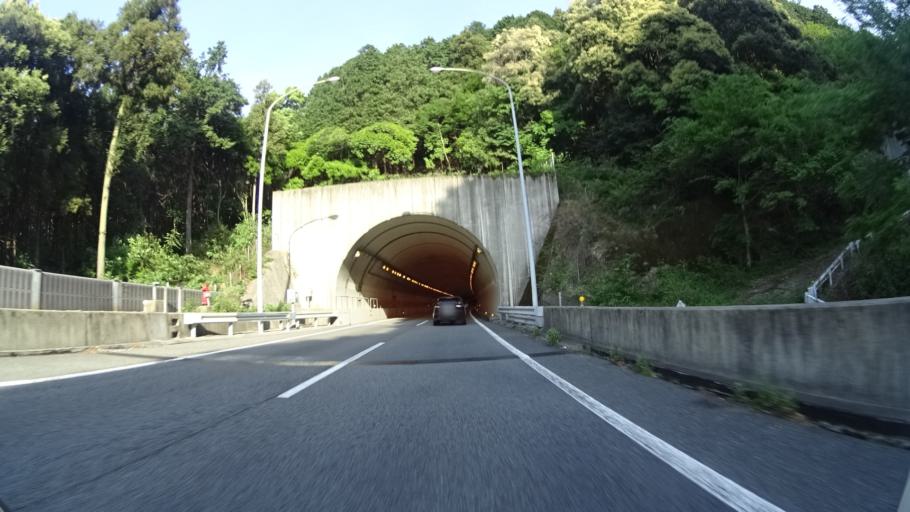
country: JP
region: Ehime
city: Niihama
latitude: 33.9173
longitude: 133.2966
